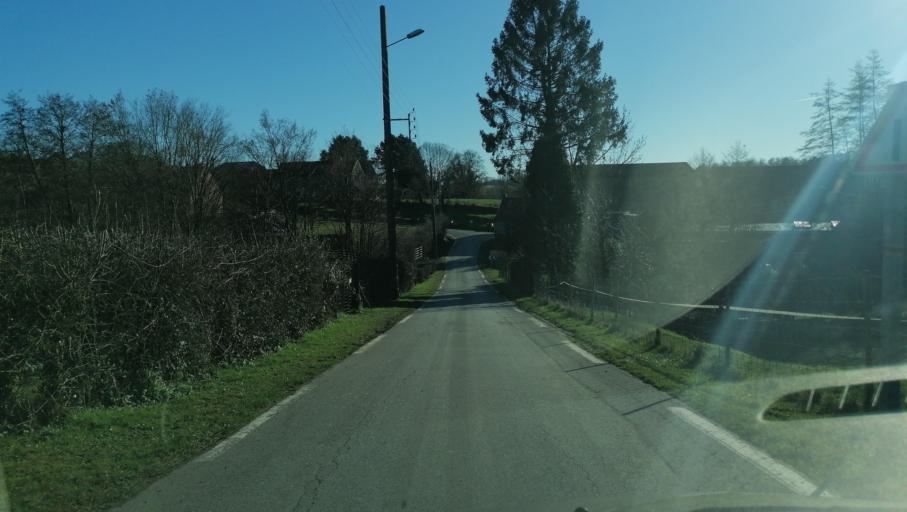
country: FR
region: Nord-Pas-de-Calais
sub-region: Departement du Nord
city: Ferriere-la-Grande
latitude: 50.2194
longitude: 4.0267
